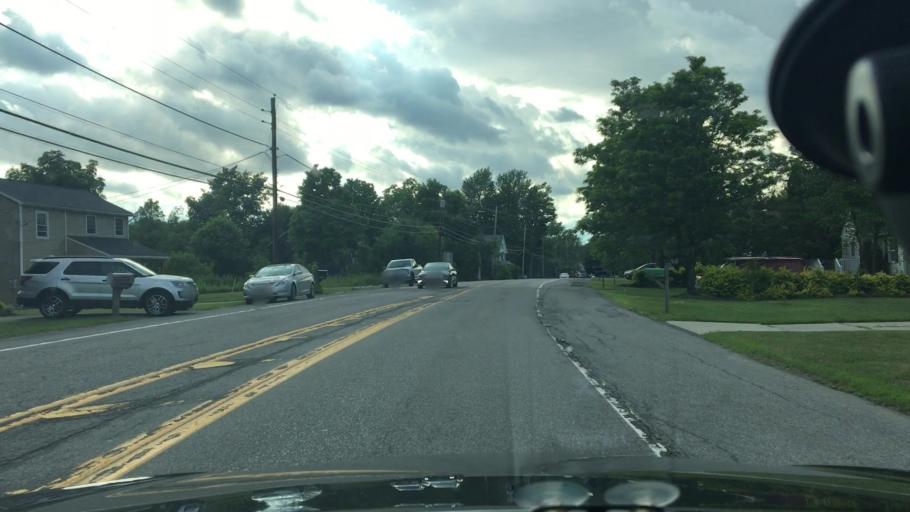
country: US
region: New York
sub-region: Erie County
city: Elma Center
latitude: 42.8278
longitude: -78.6988
